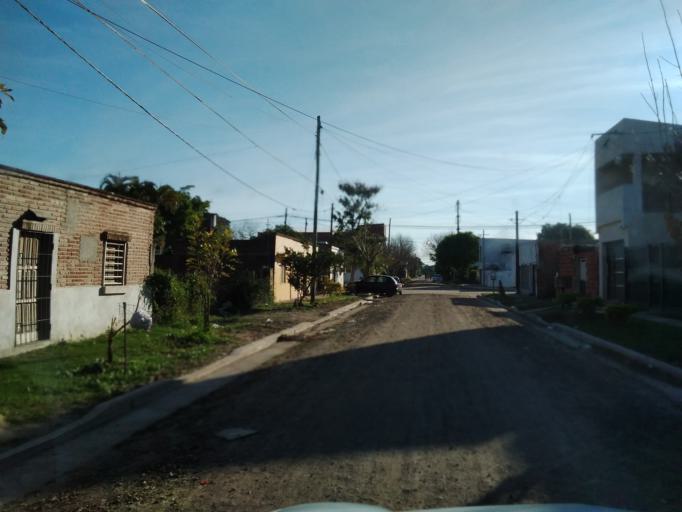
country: AR
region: Corrientes
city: Corrientes
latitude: -27.4949
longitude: -58.8364
